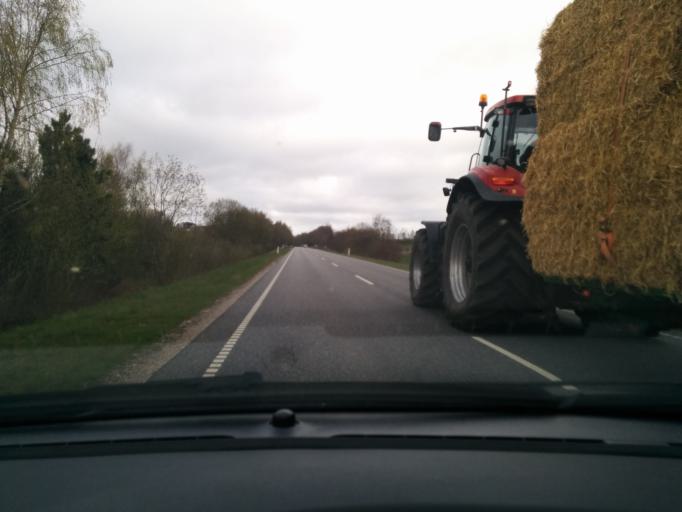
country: DK
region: Central Jutland
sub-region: Favrskov Kommune
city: Hammel
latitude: 56.2495
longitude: 9.8773
